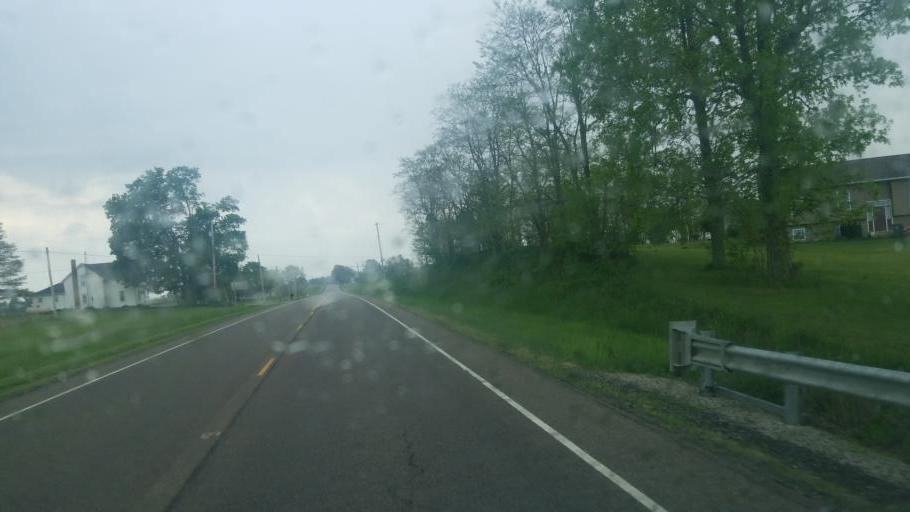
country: US
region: Ohio
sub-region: Knox County
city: Fredericktown
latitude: 40.5288
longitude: -82.5462
